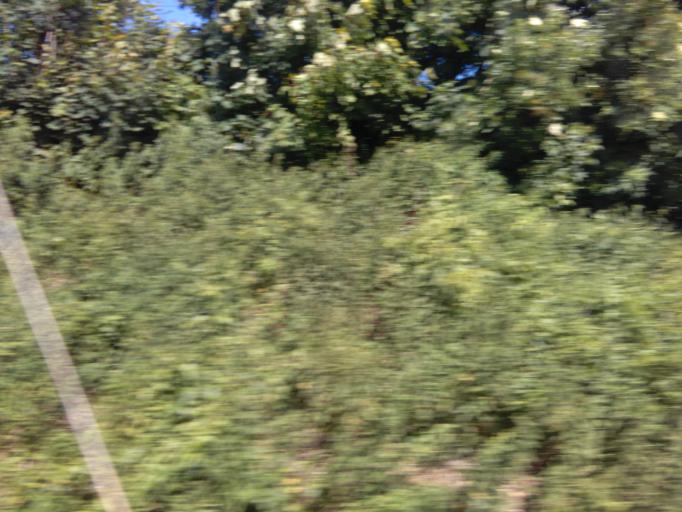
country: GB
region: England
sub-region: Luton
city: Luton
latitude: 51.8664
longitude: -0.3862
